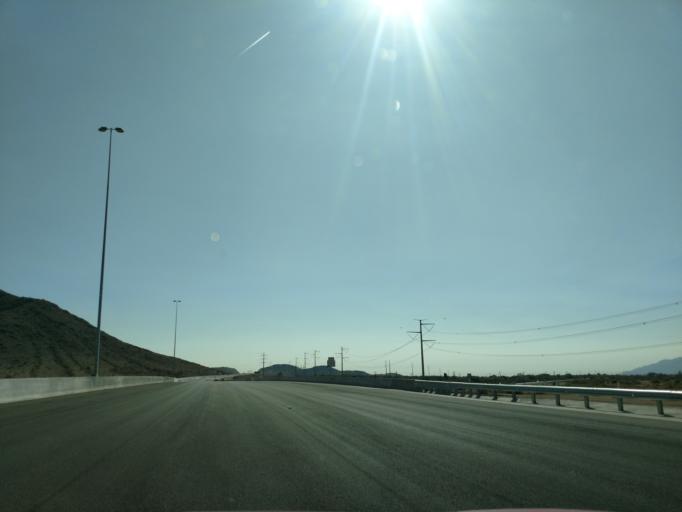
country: US
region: Arizona
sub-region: Maricopa County
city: Laveen
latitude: 33.3282
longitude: -112.1707
